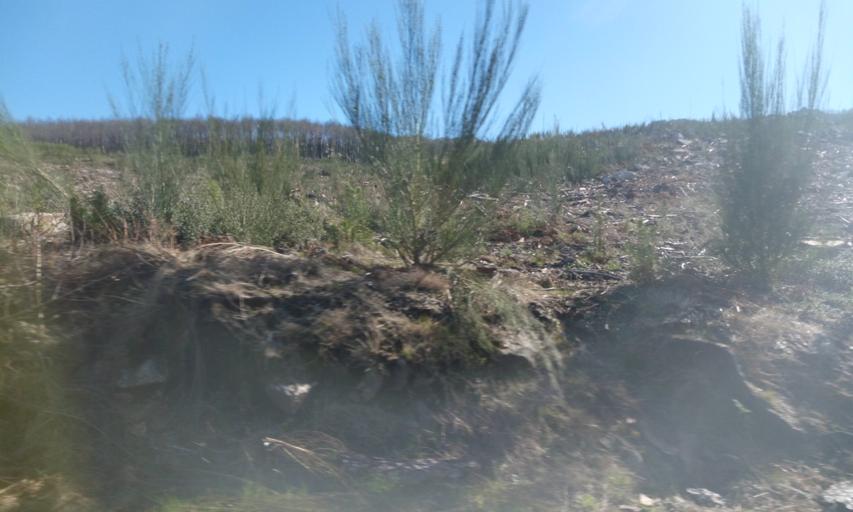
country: PT
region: Guarda
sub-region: Manteigas
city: Manteigas
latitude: 40.4920
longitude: -7.5352
